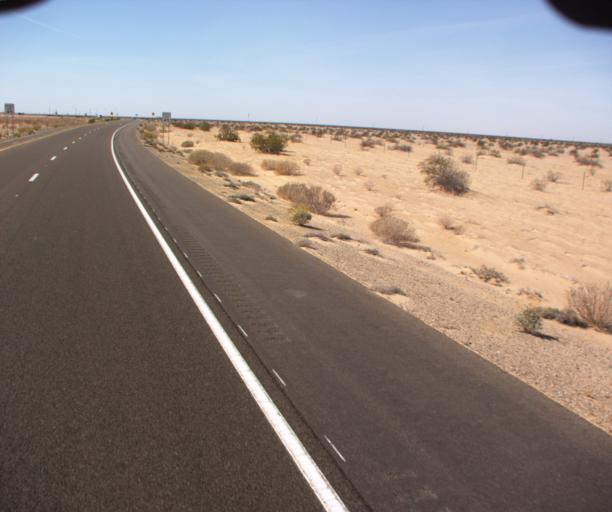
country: US
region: Arizona
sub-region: Yuma County
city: Somerton
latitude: 32.4957
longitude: -114.6413
